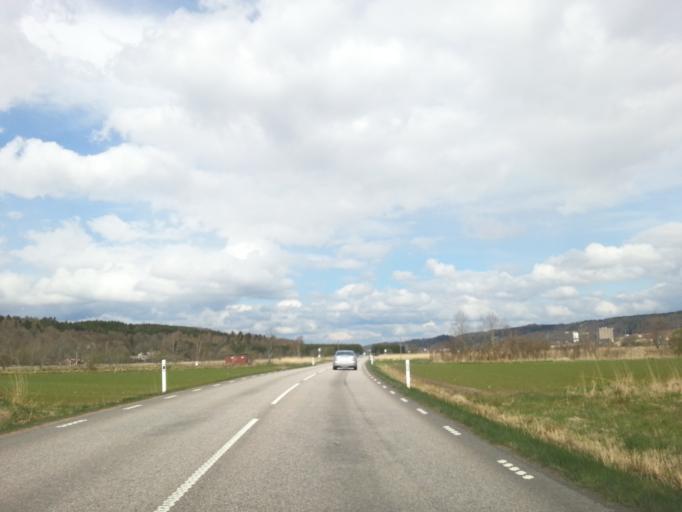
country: SE
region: Vaestra Goetaland
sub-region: Ale Kommun
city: Surte
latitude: 57.8185
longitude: 12.0001
